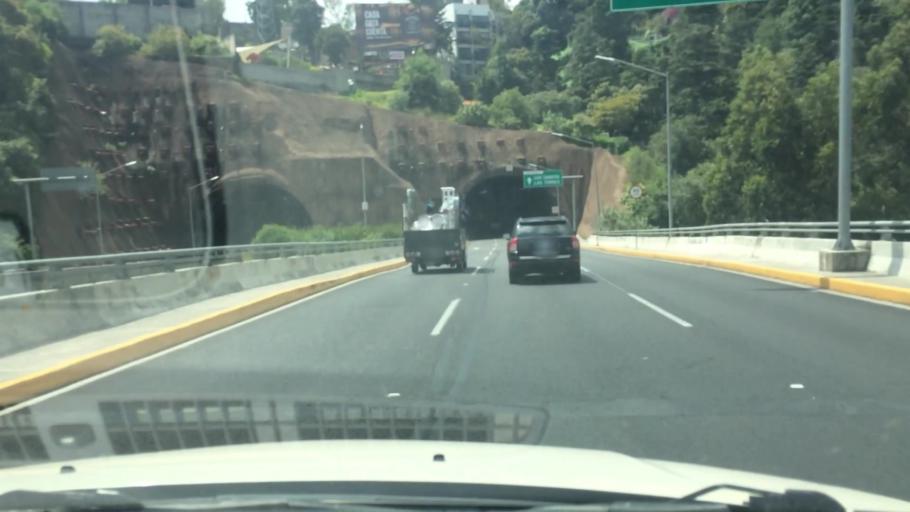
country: MX
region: Mexico City
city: Magdalena Contreras
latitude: 19.3406
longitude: -99.2403
